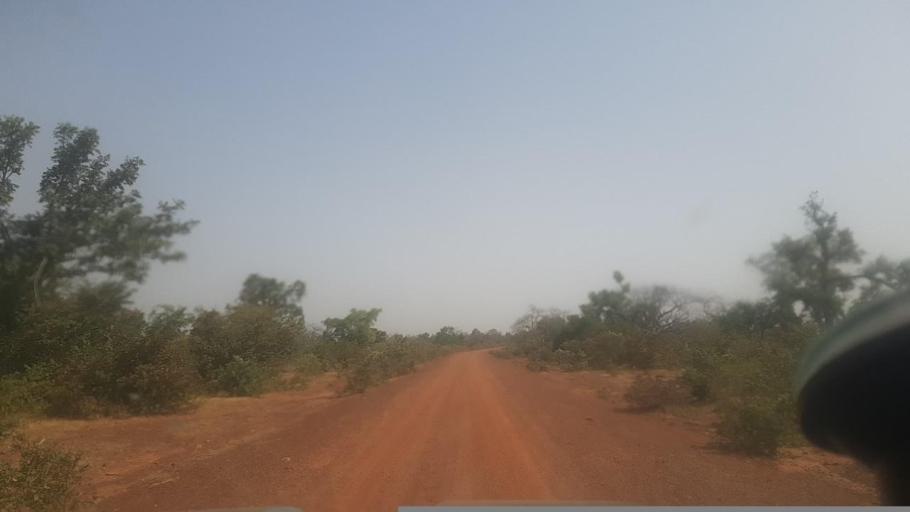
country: ML
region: Segou
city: Segou
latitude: 12.9307
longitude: -6.2824
